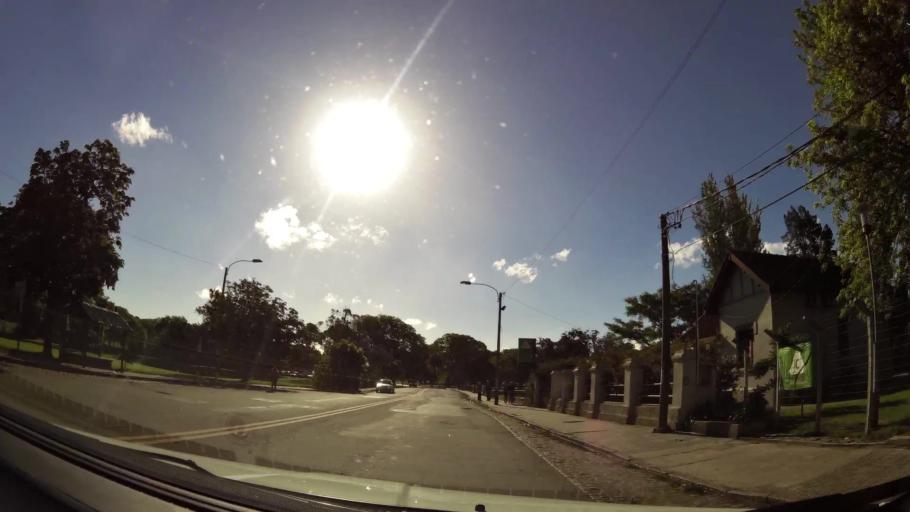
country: UY
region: Montevideo
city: Montevideo
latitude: -34.8570
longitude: -56.2018
